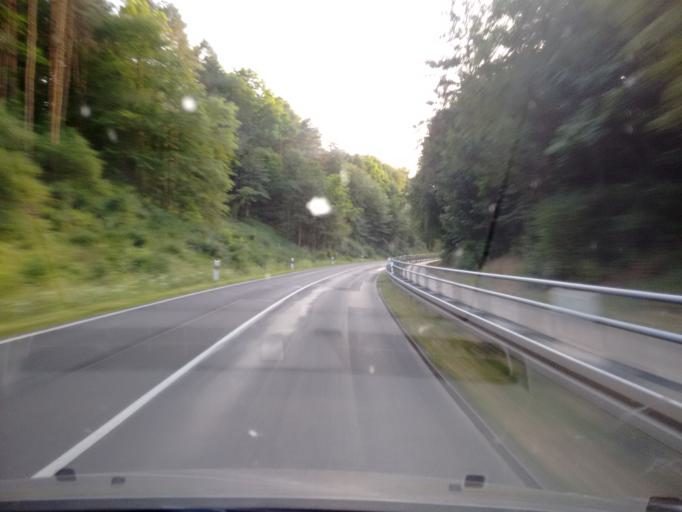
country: DE
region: Brandenburg
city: Mixdorf
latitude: 52.1327
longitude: 14.4517
